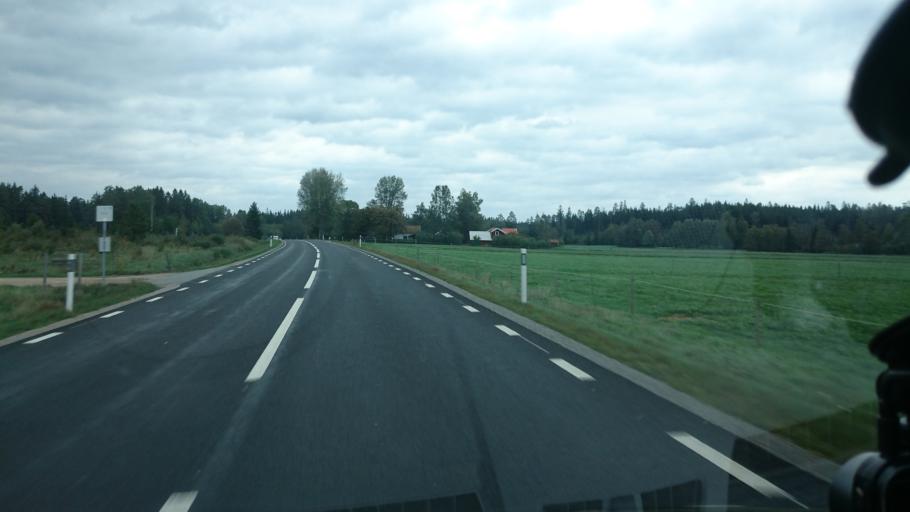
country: SE
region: Vaestra Goetaland
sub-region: Svenljunga Kommun
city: Svenljunga
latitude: 57.5495
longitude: 13.1213
